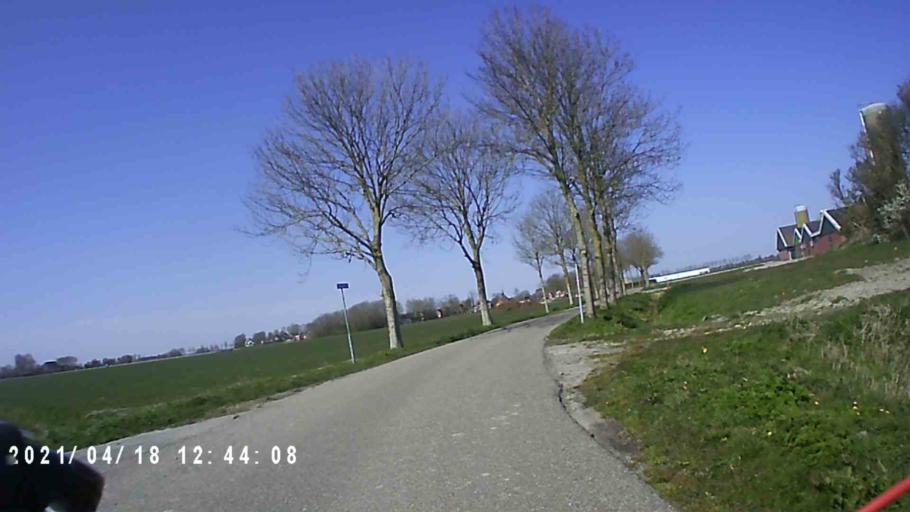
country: NL
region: Friesland
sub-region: Gemeente Dantumadiel
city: Walterswald
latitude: 53.3626
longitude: 6.0574
